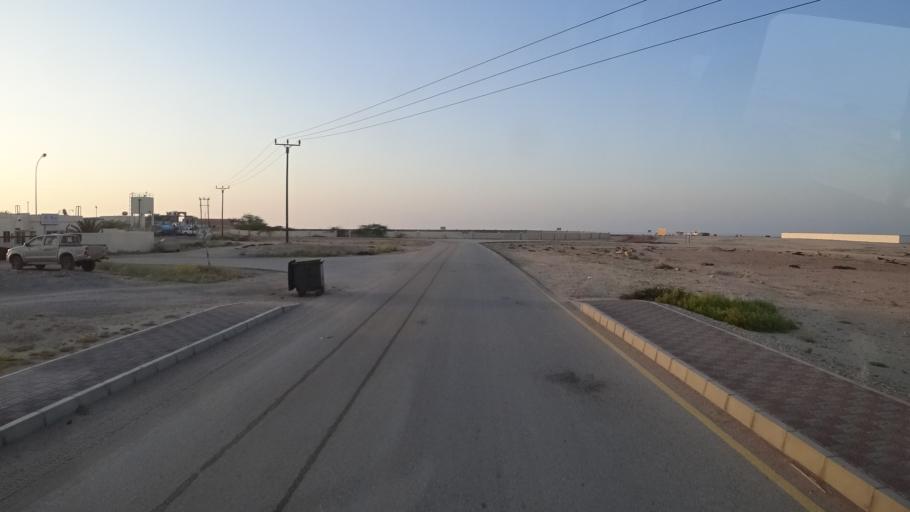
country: OM
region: Ash Sharqiyah
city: Sur
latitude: 22.5291
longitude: 59.7642
